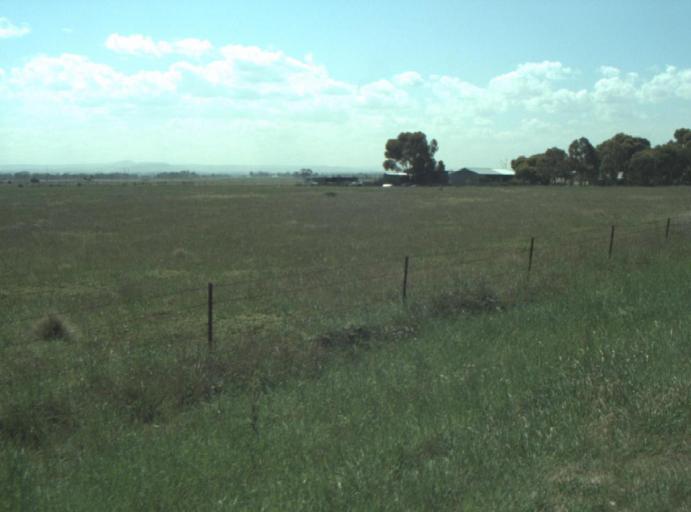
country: AU
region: Victoria
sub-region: Greater Geelong
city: Lara
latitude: -38.0035
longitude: 144.3998
